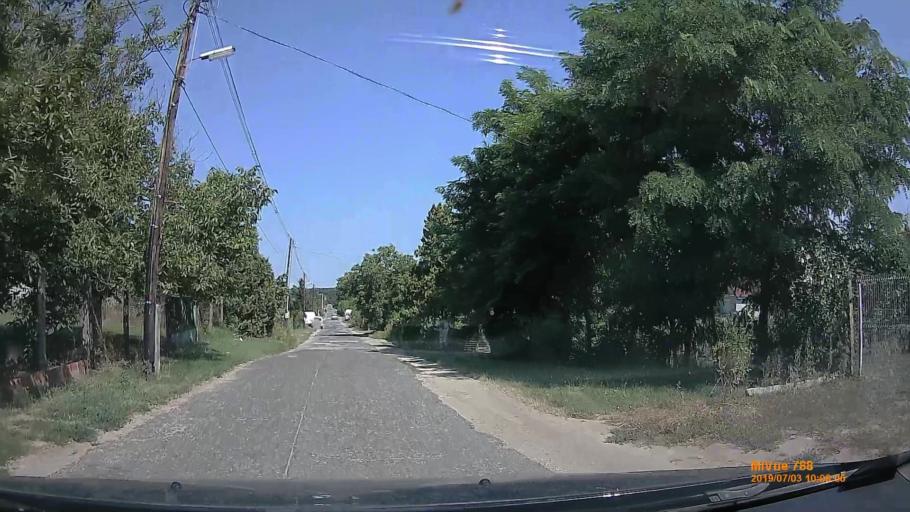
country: HU
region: Gyor-Moson-Sopron
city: Gyor
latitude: 47.7193
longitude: 17.7140
